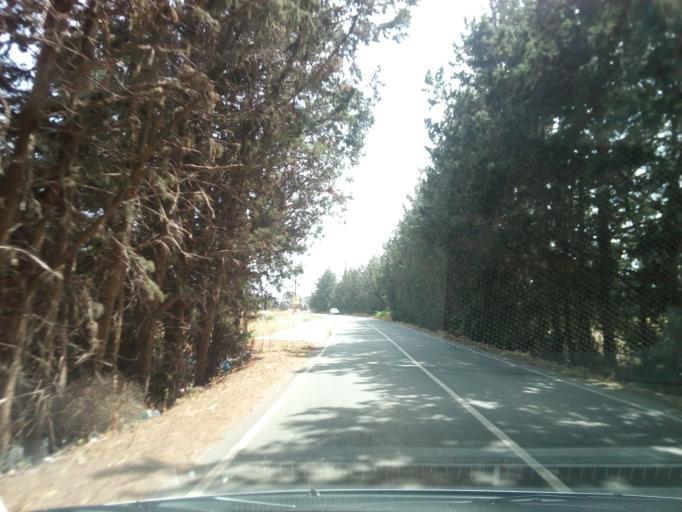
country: CY
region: Larnaka
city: Meneou
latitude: 34.8583
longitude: 33.5958
